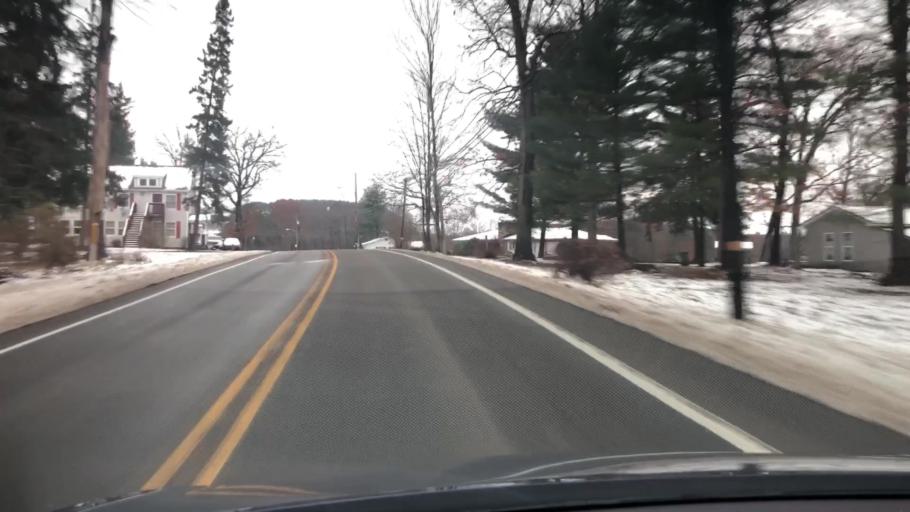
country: US
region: Pennsylvania
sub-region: Clarion County
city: Clarion
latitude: 41.0260
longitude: -79.2652
